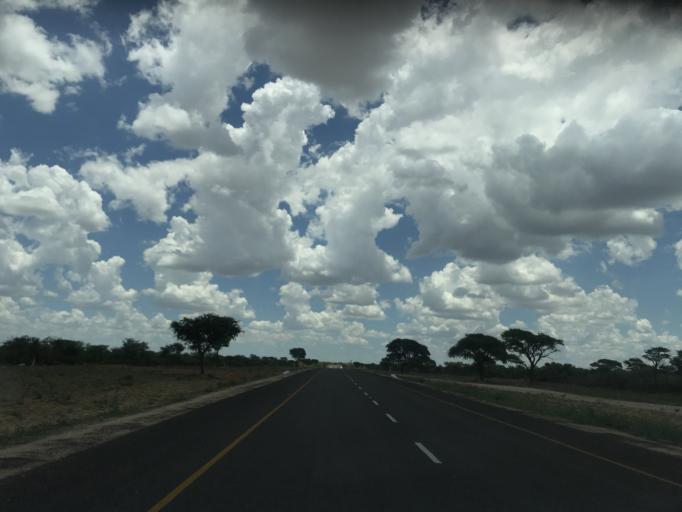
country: BW
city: Mabuli
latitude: -25.8030
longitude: 24.8362
